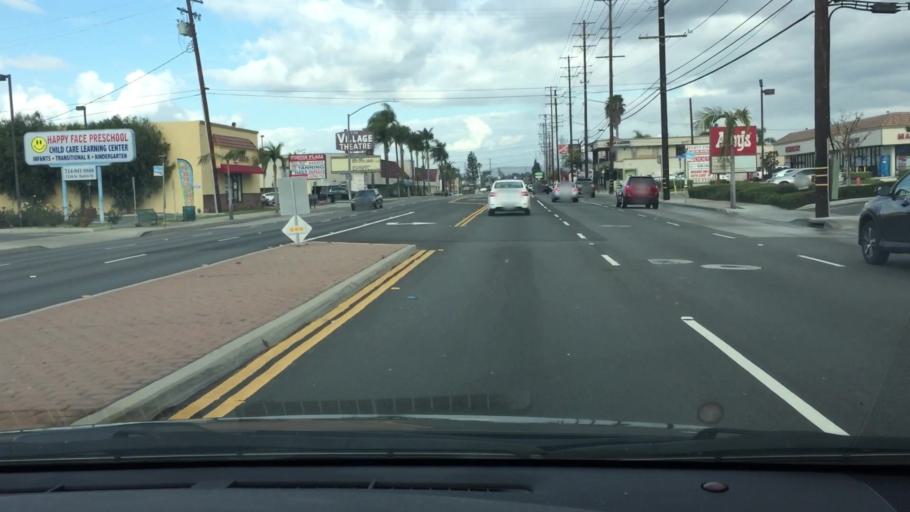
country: US
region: California
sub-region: Orange County
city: Villa Park
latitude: 33.8058
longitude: -117.8357
